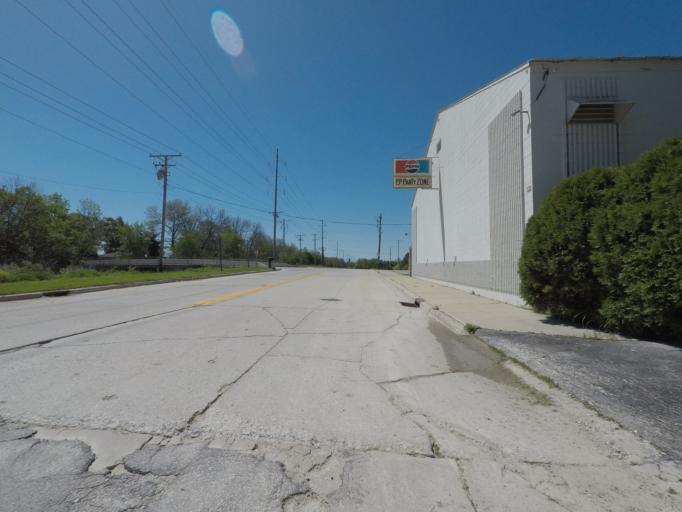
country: US
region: Wisconsin
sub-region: Sheboygan County
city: Sheboygan
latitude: 43.7548
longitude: -87.7296
